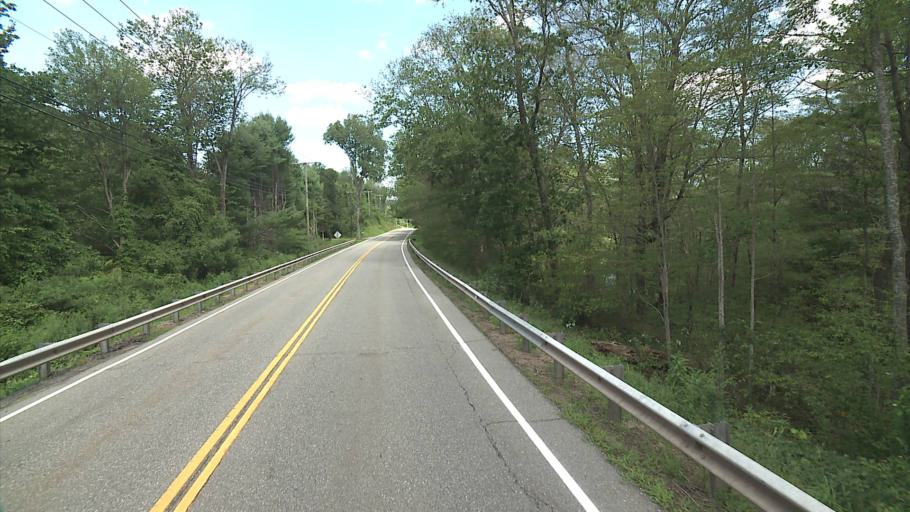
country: US
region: Connecticut
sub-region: Tolland County
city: Storrs
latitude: 41.8458
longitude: -72.0960
